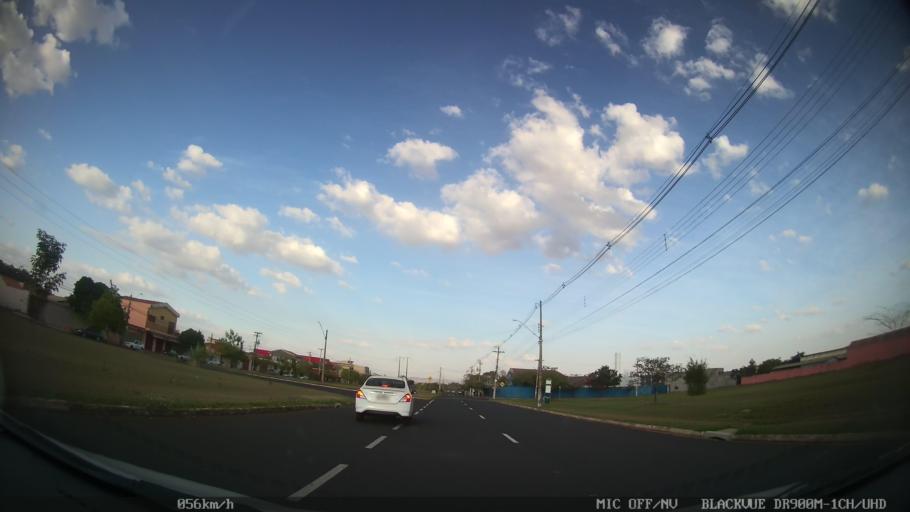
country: BR
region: Sao Paulo
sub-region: Ribeirao Preto
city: Ribeirao Preto
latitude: -21.1942
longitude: -47.7372
